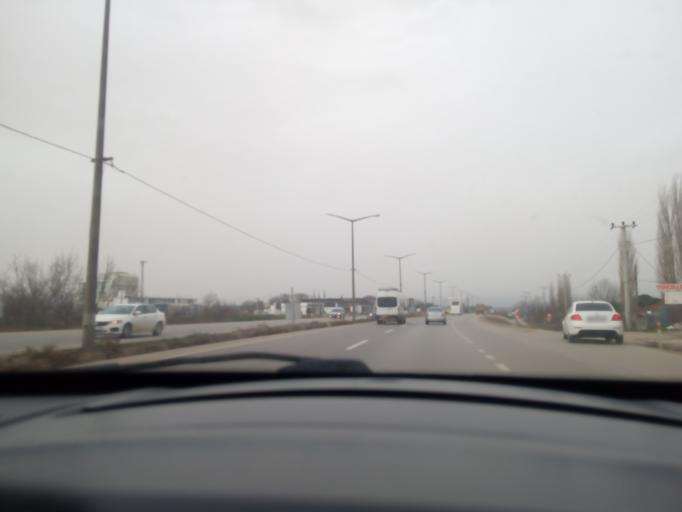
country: TR
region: Bursa
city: Tatkavakli
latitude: 40.0327
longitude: 28.3688
